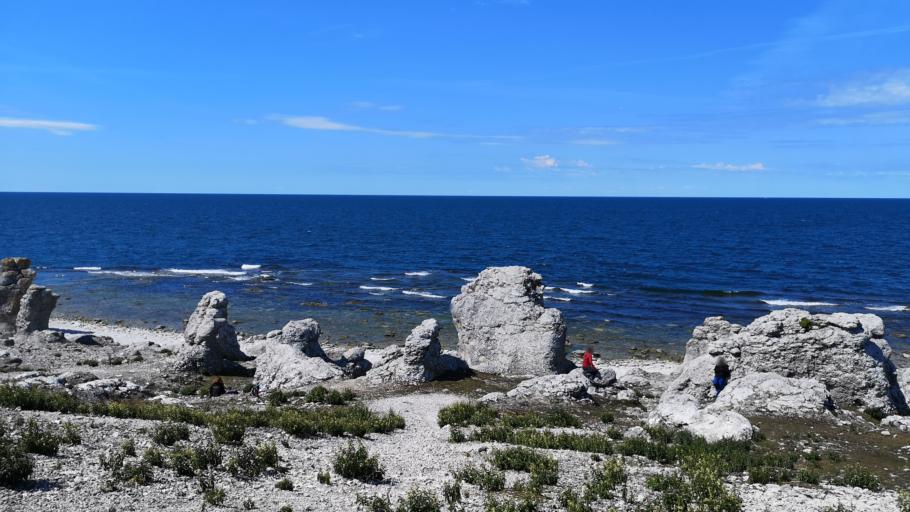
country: SE
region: Gotland
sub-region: Gotland
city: Slite
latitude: 57.9976
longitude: 19.1819
